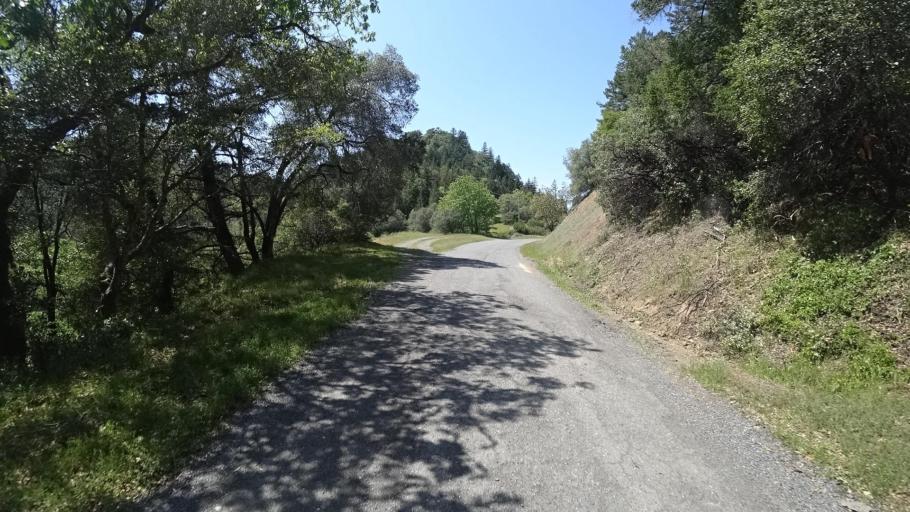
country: US
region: California
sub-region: Humboldt County
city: Redway
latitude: 40.2299
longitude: -123.6470
